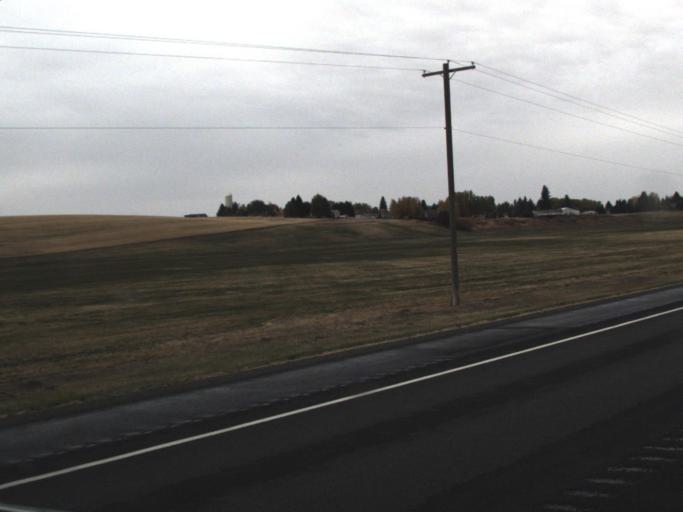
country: US
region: Washington
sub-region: Asotin County
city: Clarkston
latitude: 46.5633
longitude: -117.1115
